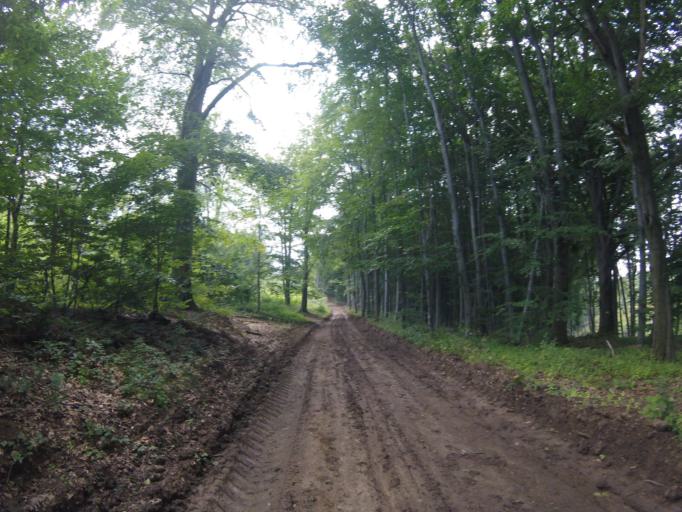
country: SK
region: Nitriansky
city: Sahy
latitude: 47.9539
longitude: 18.8891
